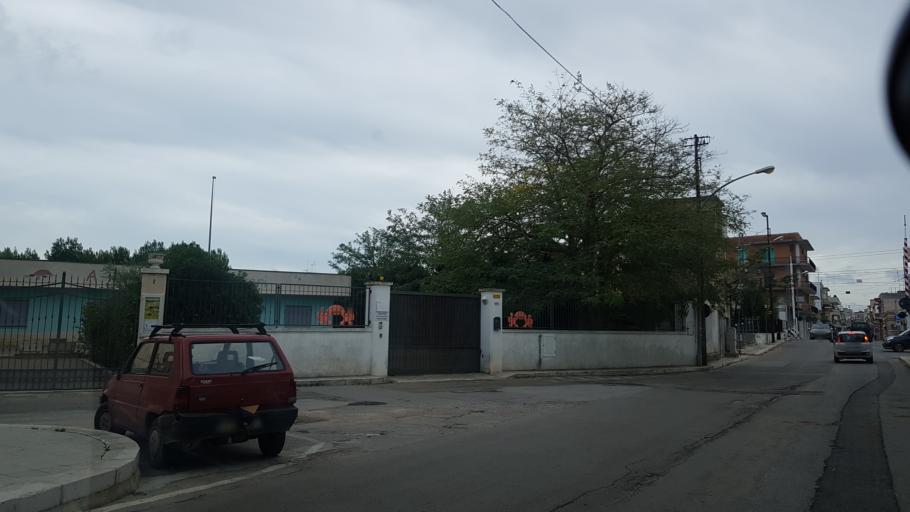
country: IT
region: Apulia
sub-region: Provincia di Brindisi
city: Mesagne
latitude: 40.5647
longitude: 17.8034
